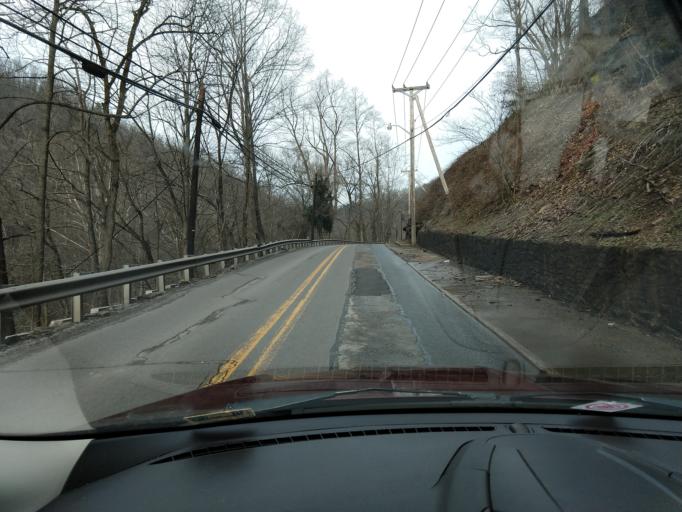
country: US
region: West Virginia
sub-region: McDowell County
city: Welch
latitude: 37.4227
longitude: -81.5861
